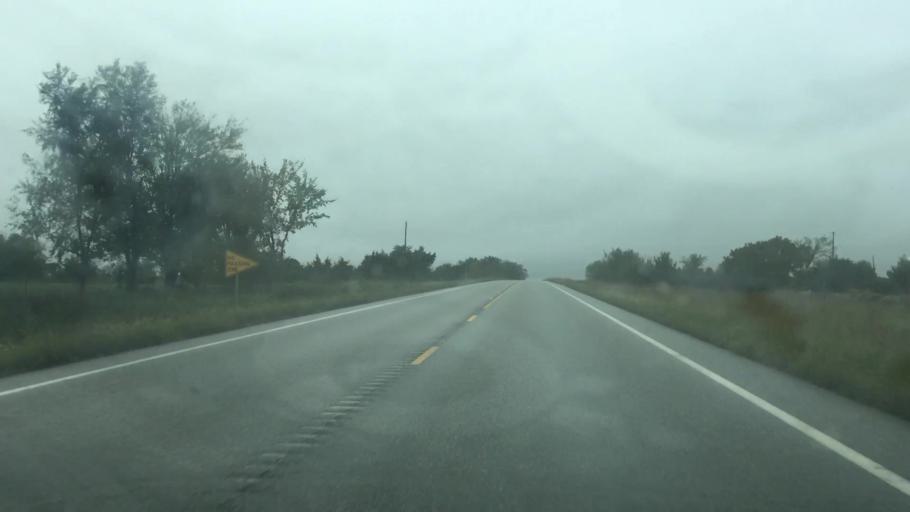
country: US
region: Kansas
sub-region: Anderson County
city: Garnett
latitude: 38.2997
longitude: -95.1961
